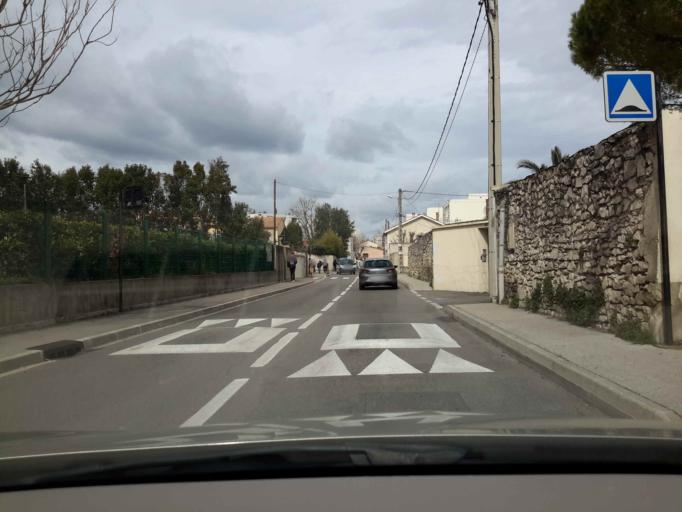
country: FR
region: Languedoc-Roussillon
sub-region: Departement du Gard
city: Nimes
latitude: 43.8257
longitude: 4.3653
